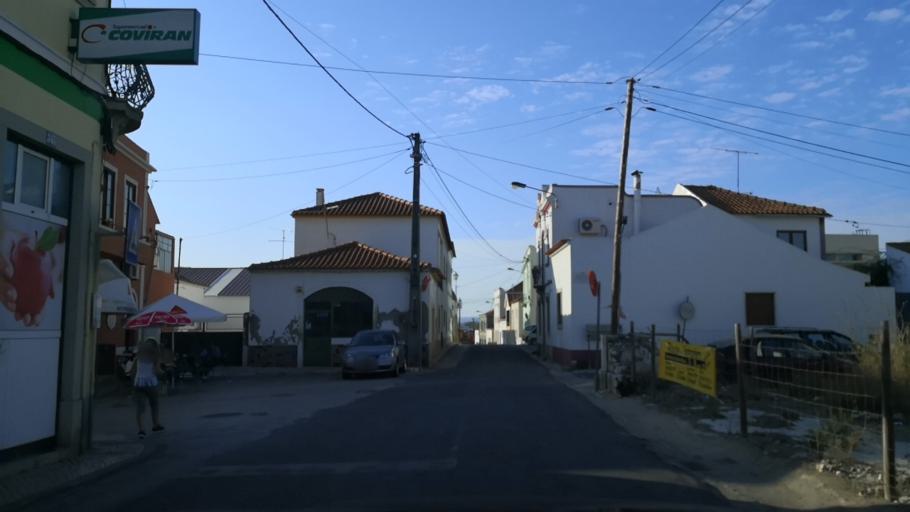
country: PT
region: Santarem
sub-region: Santarem
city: Santarem
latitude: 39.2977
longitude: -8.6598
